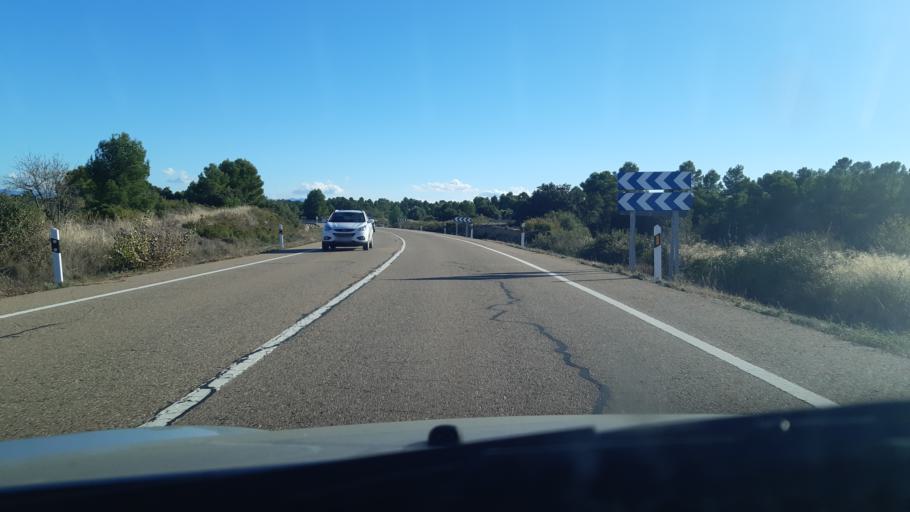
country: ES
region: Aragon
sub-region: Provincia de Teruel
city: Valdealgorfa
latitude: 40.9549
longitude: -0.0151
